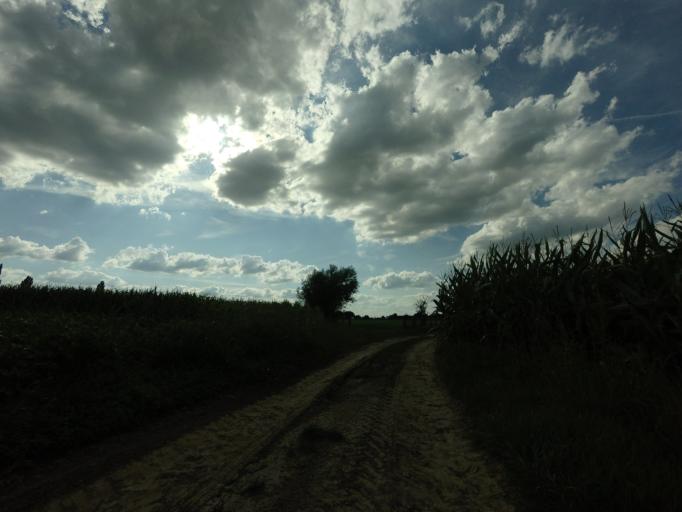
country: BE
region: Flanders
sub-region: Provincie Vlaams-Brabant
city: Grimbergen
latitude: 50.9516
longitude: 4.3520
